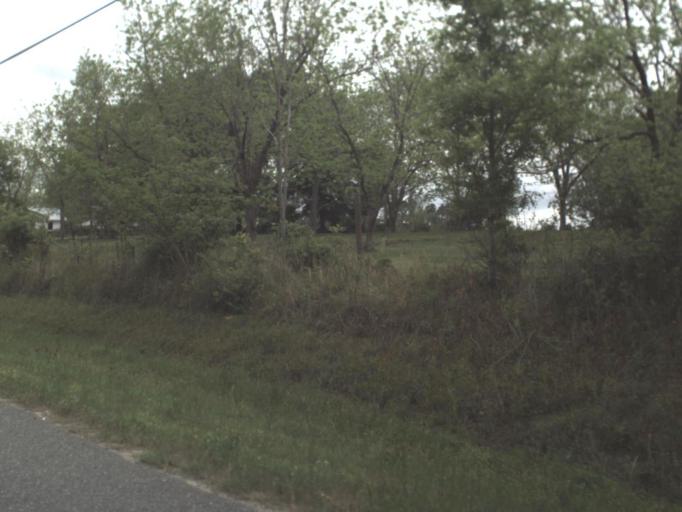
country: US
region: Florida
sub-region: Santa Rosa County
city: Point Baker
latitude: 30.8401
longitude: -87.0503
